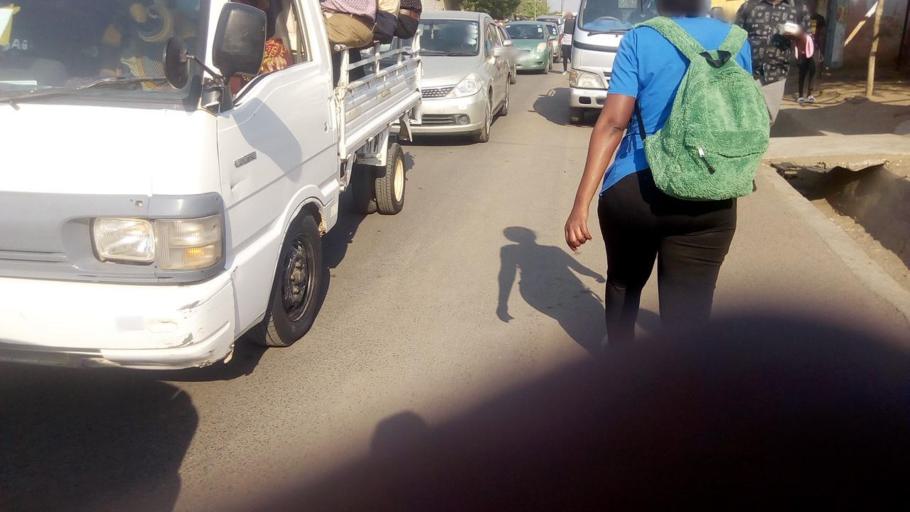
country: ZM
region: Lusaka
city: Lusaka
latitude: -15.3710
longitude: 28.2931
